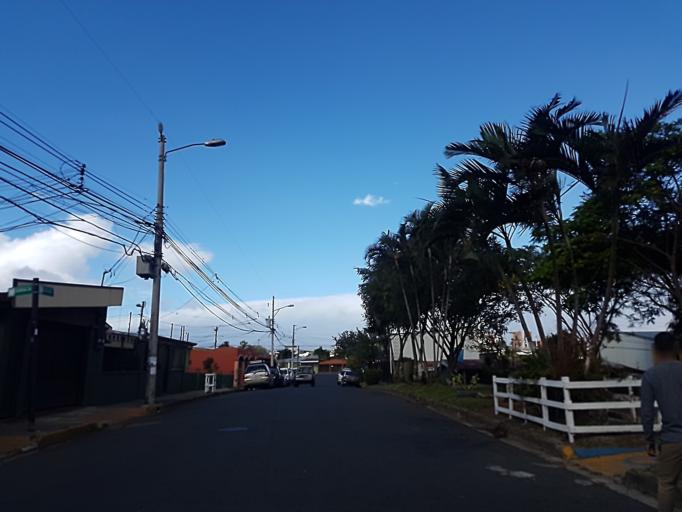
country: CR
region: San Jose
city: San Felipe
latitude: 9.9212
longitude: -84.0985
